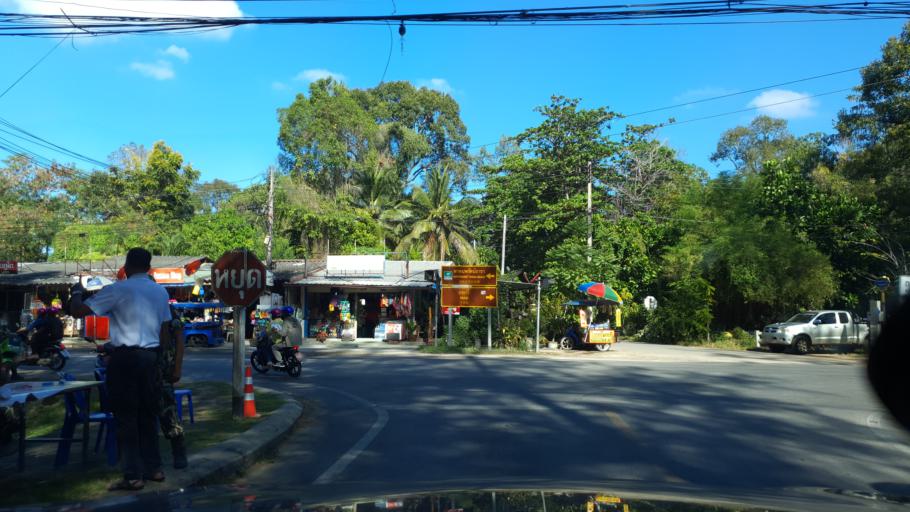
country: TH
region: Phangnga
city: Ban Ao Nang
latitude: 8.0473
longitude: 98.8015
